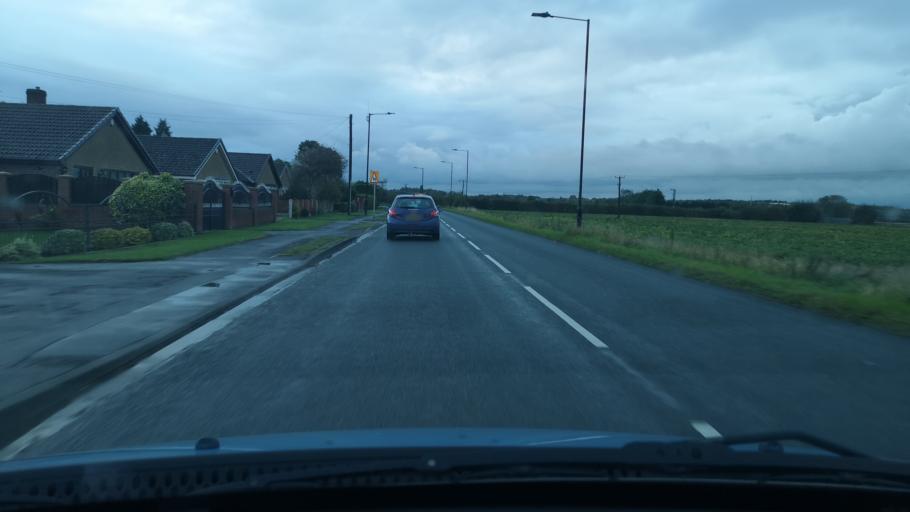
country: GB
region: England
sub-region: Doncaster
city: Askern
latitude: 53.6193
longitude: -1.1336
